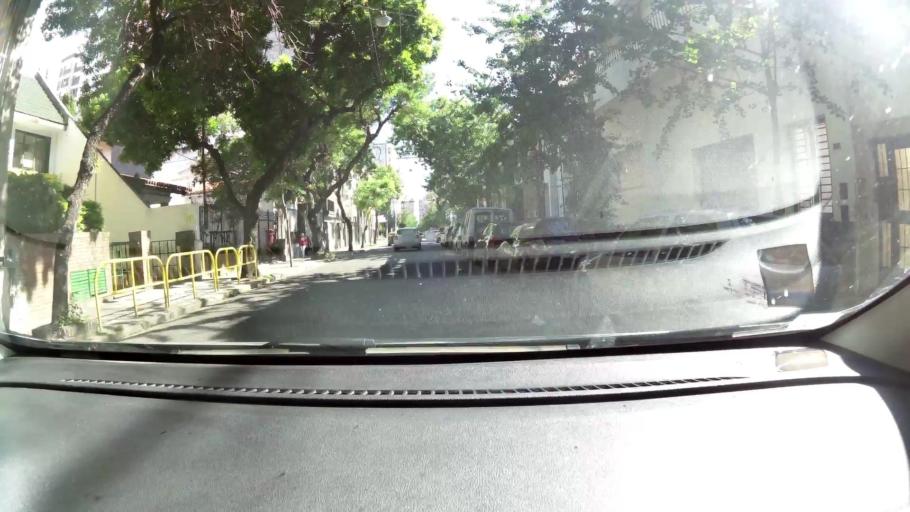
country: AR
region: Santa Fe
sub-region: Departamento de Rosario
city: Rosario
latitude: -32.9538
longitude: -60.6312
